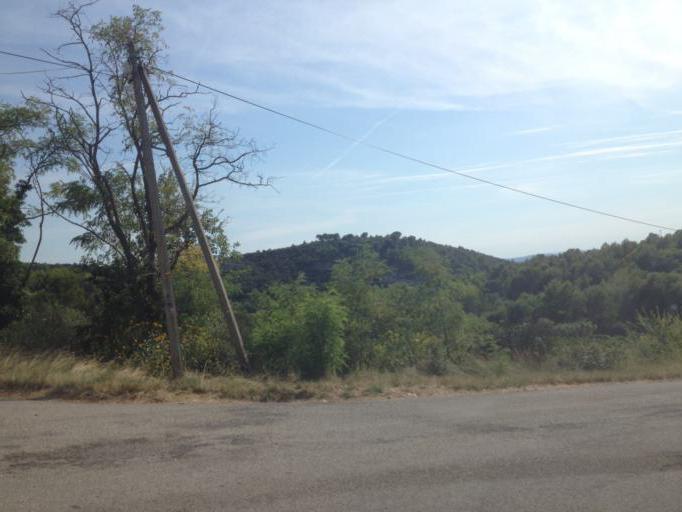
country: FR
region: Provence-Alpes-Cote d'Azur
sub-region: Departement du Vaucluse
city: Vacqueyras
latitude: 44.1362
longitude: 5.0055
